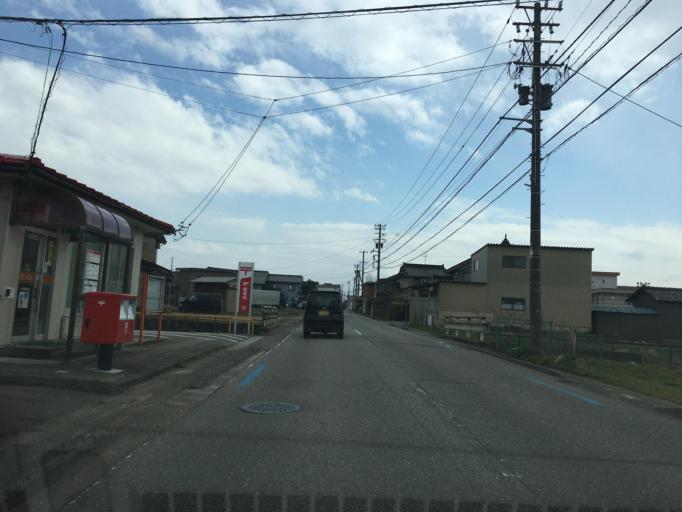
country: JP
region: Toyama
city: Kuragaki-kosugi
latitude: 36.6849
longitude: 137.1198
